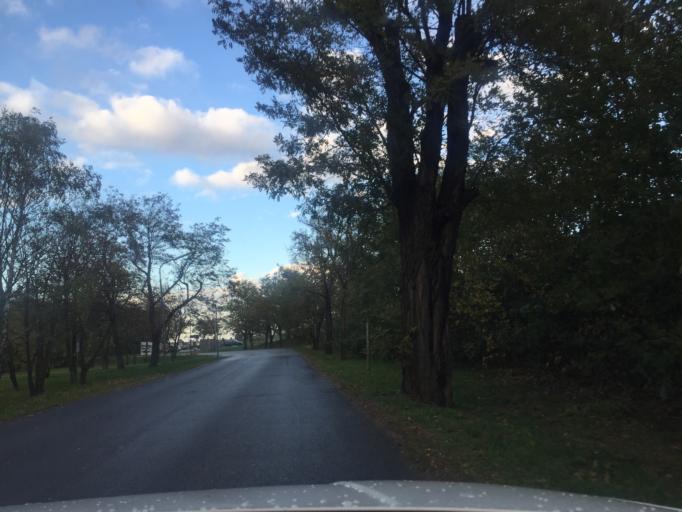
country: AT
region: Lower Austria
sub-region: Politischer Bezirk Wien-Umgebung
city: Gerasdorf bei Wien
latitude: 48.2806
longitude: 16.4605
